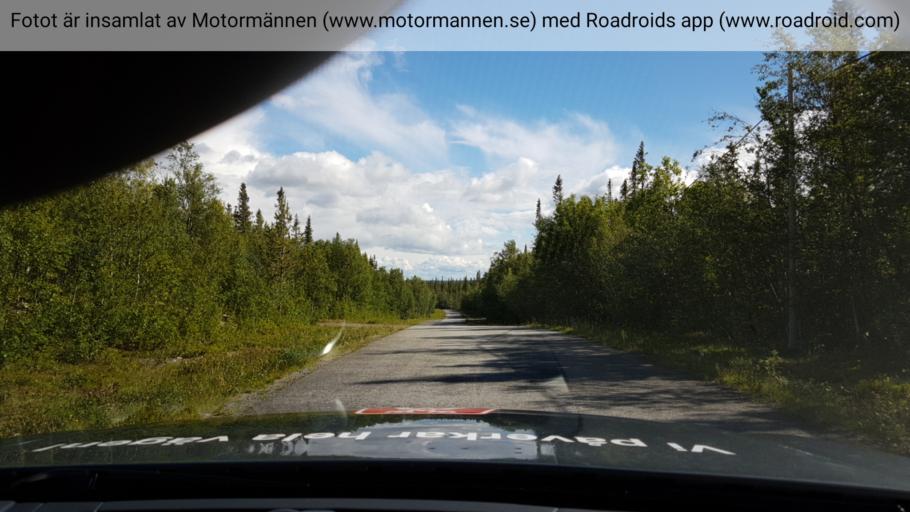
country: SE
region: Jaemtland
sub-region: Bergs Kommun
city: Hoverberg
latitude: 63.0114
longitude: 13.9419
